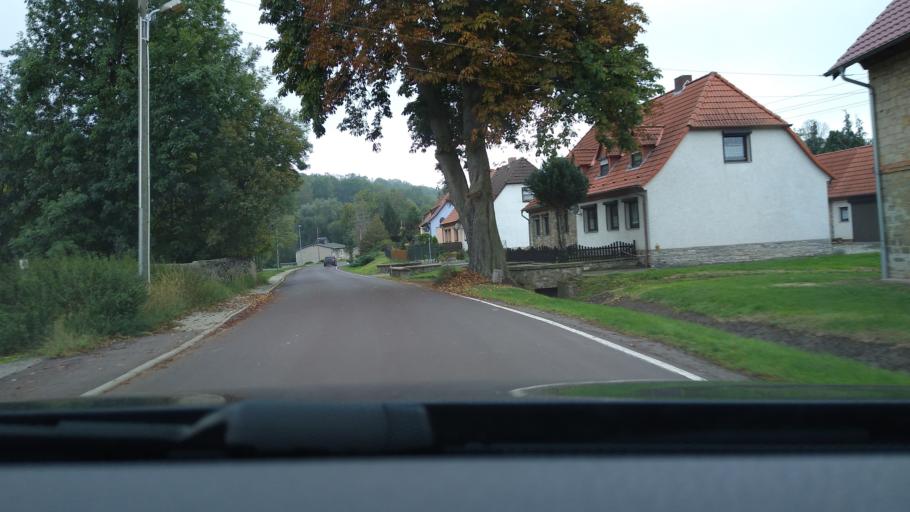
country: DE
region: Saxony-Anhalt
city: Polleben
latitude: 51.6031
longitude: 11.6144
